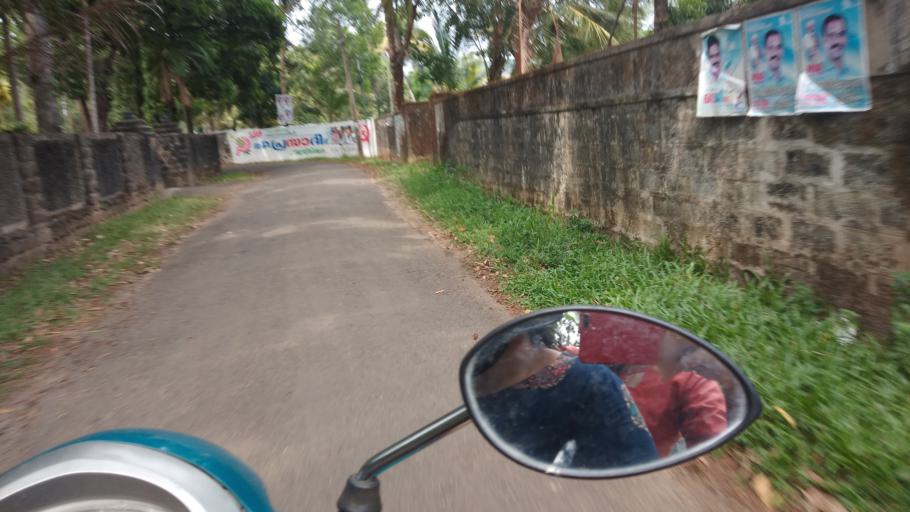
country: IN
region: Kerala
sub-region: Alappuzha
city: Shertallai
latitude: 9.6066
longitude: 76.3637
